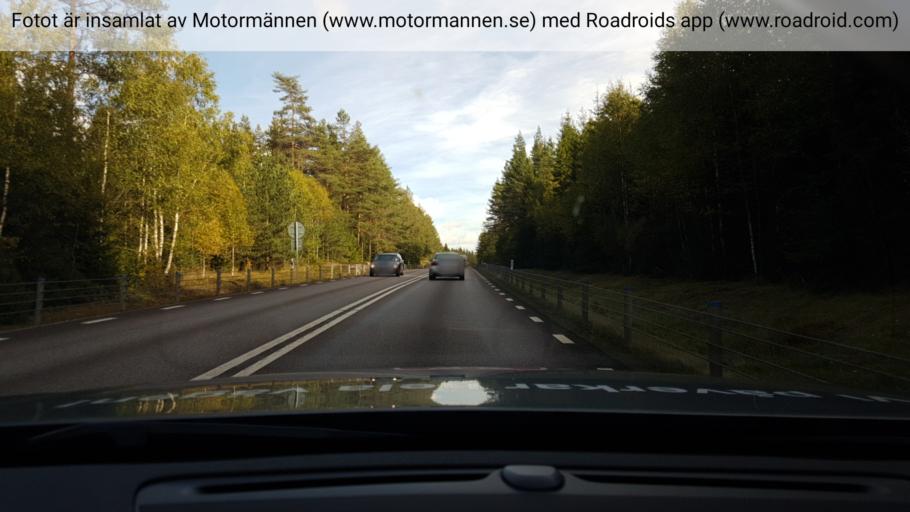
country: SE
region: Vaermland
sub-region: Arjangs Kommun
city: Toecksfors
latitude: 59.4980
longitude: 11.9019
